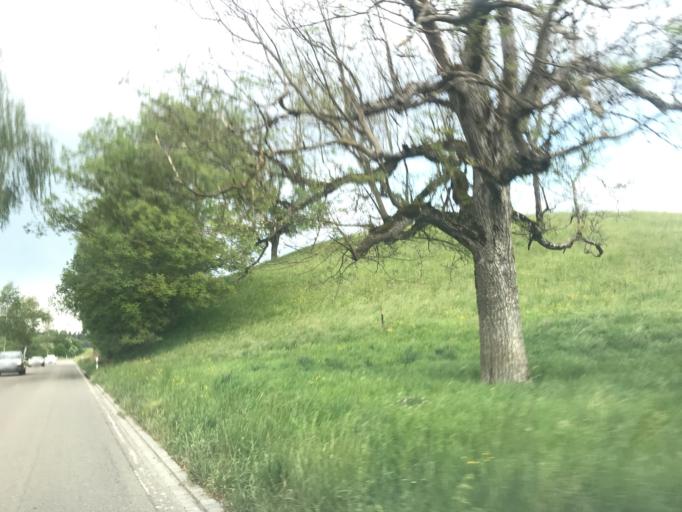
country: CH
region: Zurich
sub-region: Bezirk Winterthur
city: Wuelflingen (Kreis 6) / Niederfeld
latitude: 47.4977
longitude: 8.6731
